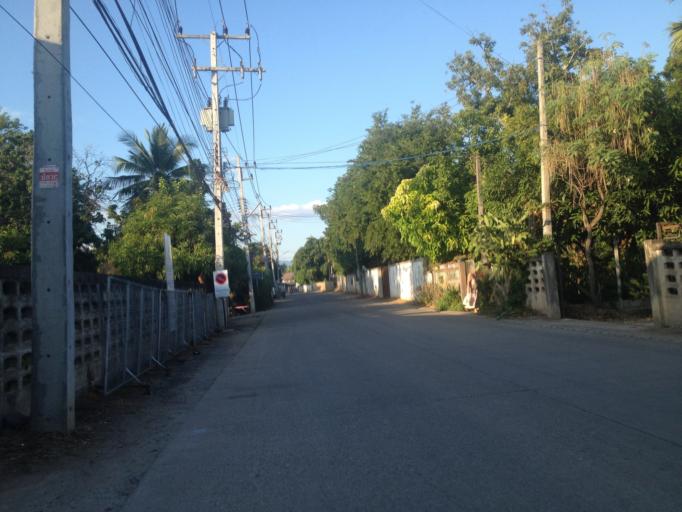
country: TH
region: Chiang Mai
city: San Pa Tong
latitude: 18.6255
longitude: 98.8942
